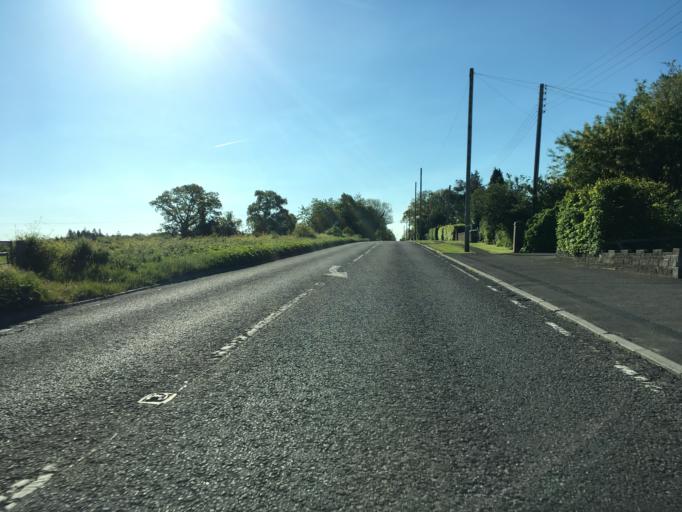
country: GB
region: England
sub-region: North Somerset
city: Easton-in-Gordano
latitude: 51.4433
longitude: -2.6949
